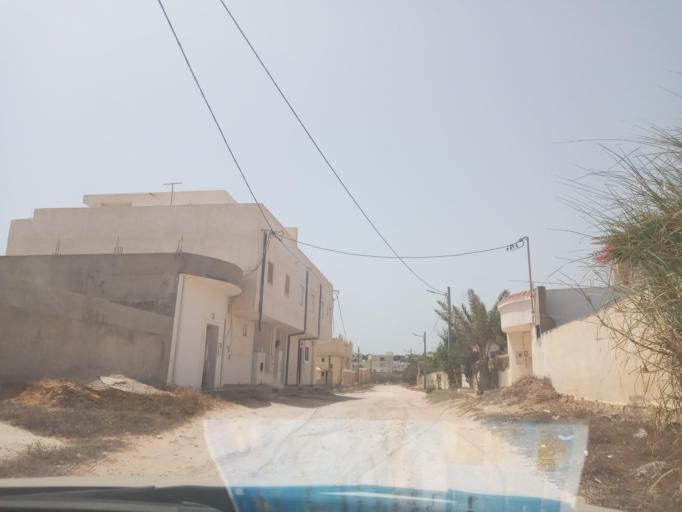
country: TN
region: Nabul
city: El Haouaria
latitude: 37.0283
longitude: 11.0562
